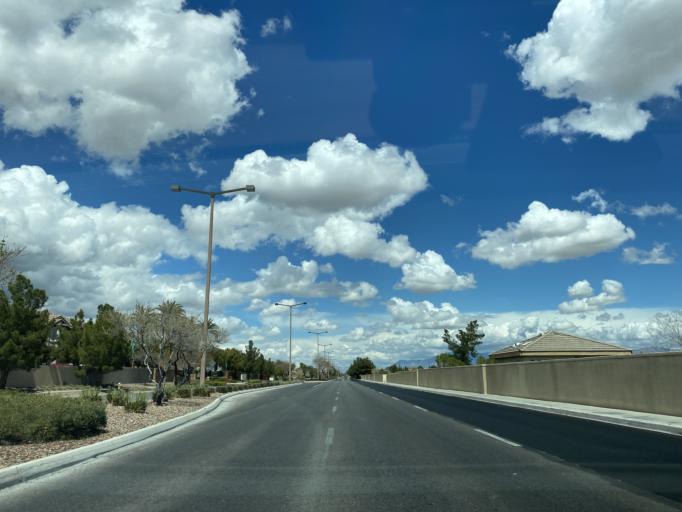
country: US
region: Nevada
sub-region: Clark County
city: Summerlin South
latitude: 36.1617
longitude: -115.3143
